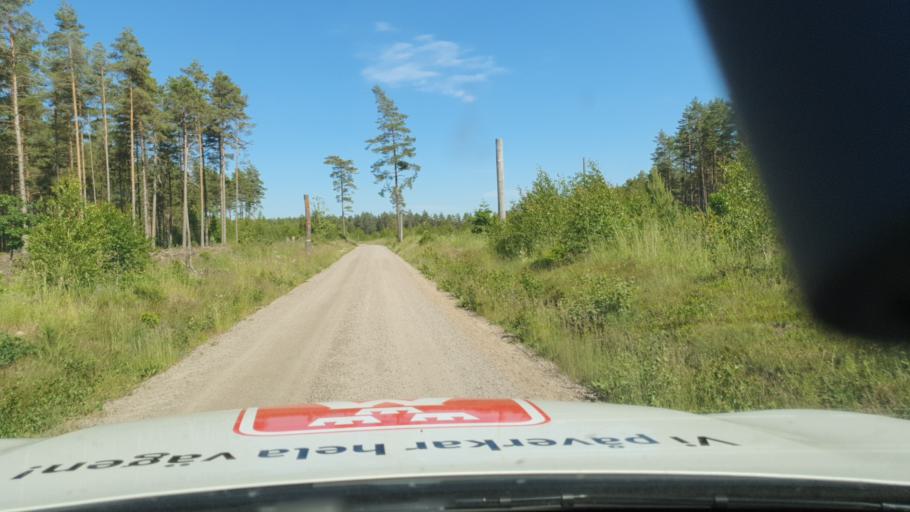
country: SE
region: Vaestra Goetaland
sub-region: Skovde Kommun
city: Skultorp
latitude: 58.3116
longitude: 13.8507
